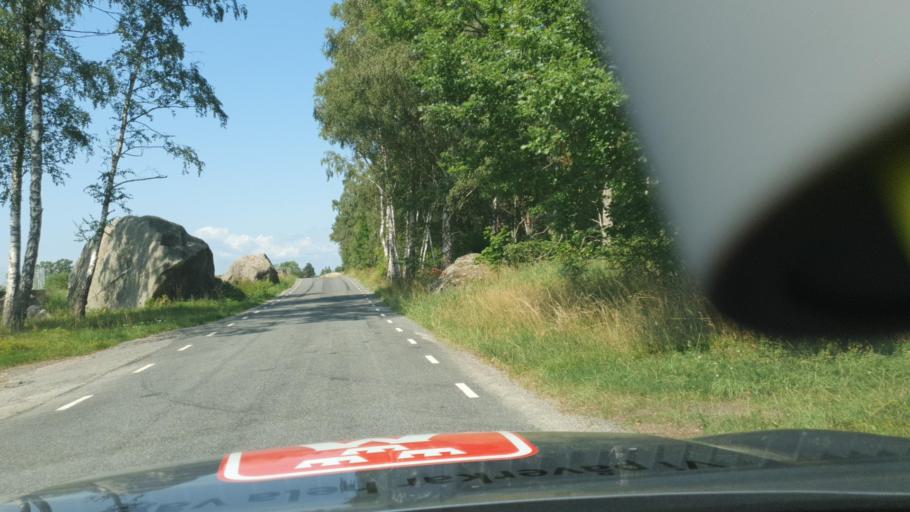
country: SE
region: Skane
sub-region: Kristianstads Kommun
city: Fjalkinge
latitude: 56.0638
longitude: 14.3655
